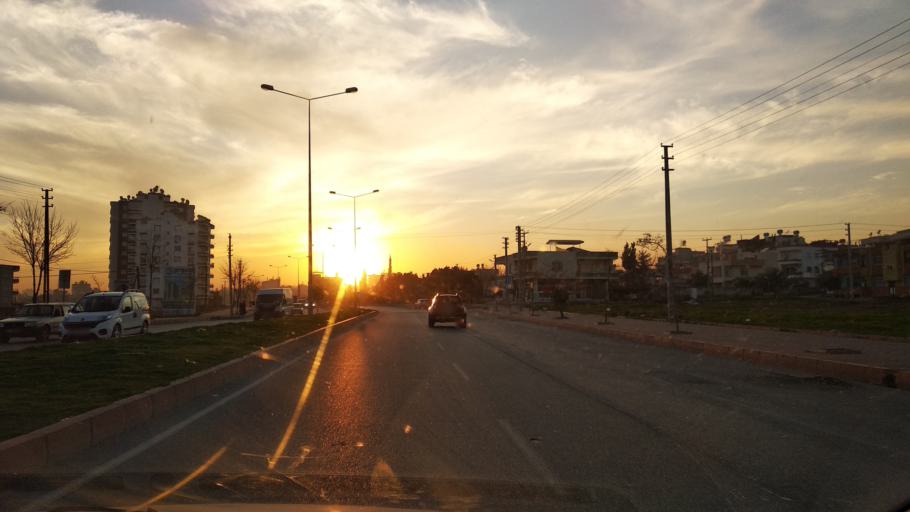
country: TR
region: Mersin
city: Mercin
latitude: 36.8305
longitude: 34.6129
